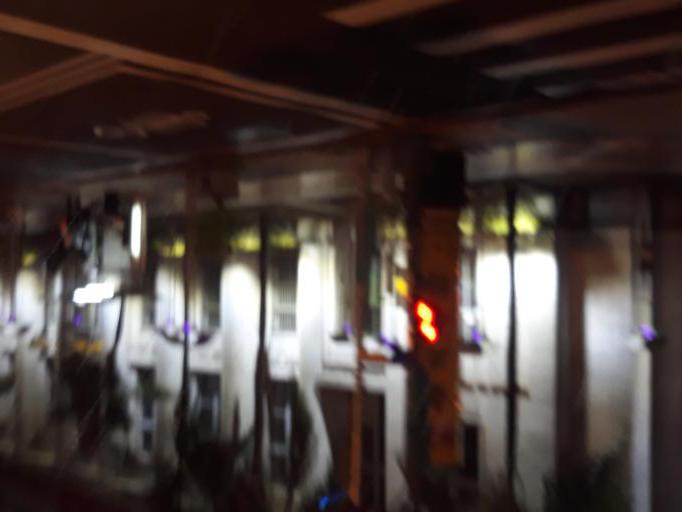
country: TW
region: Taiwan
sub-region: Taichung City
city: Taichung
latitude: 24.1400
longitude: 120.6823
